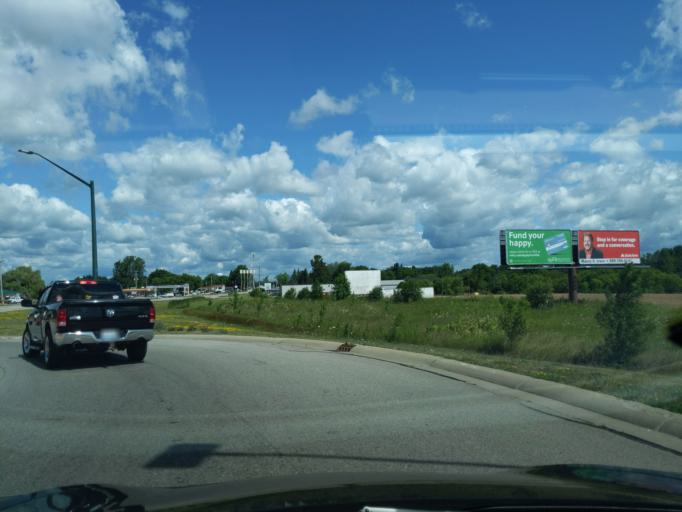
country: US
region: Michigan
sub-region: Clare County
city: Clare
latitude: 43.8088
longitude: -84.7674
